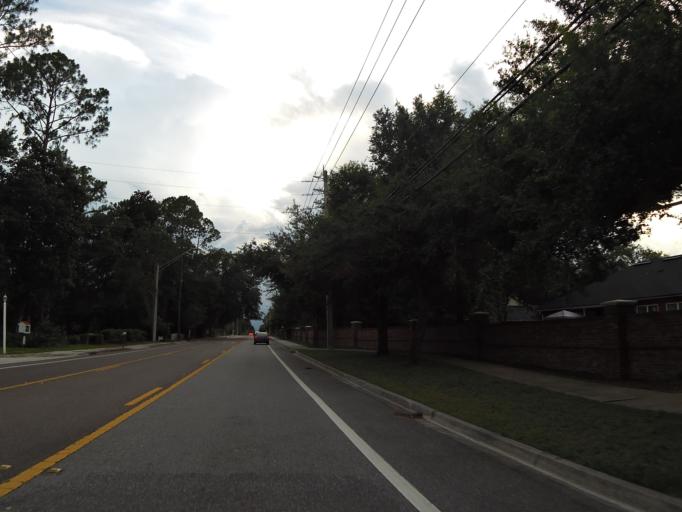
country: US
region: Florida
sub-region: Clay County
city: Bellair-Meadowbrook Terrace
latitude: 30.3023
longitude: -81.8062
